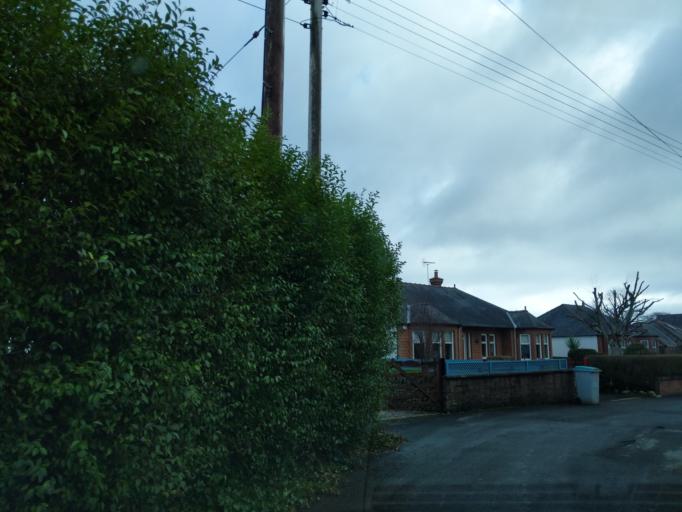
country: GB
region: Scotland
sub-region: Dumfries and Galloway
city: Moffat
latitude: 55.3364
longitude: -3.4327
